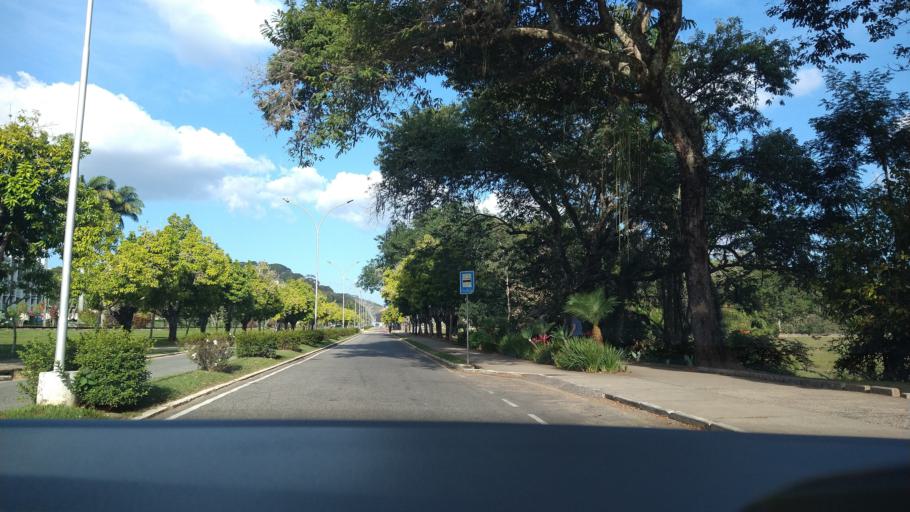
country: BR
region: Minas Gerais
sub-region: Vicosa
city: Vicosa
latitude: -20.7593
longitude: -42.8715
